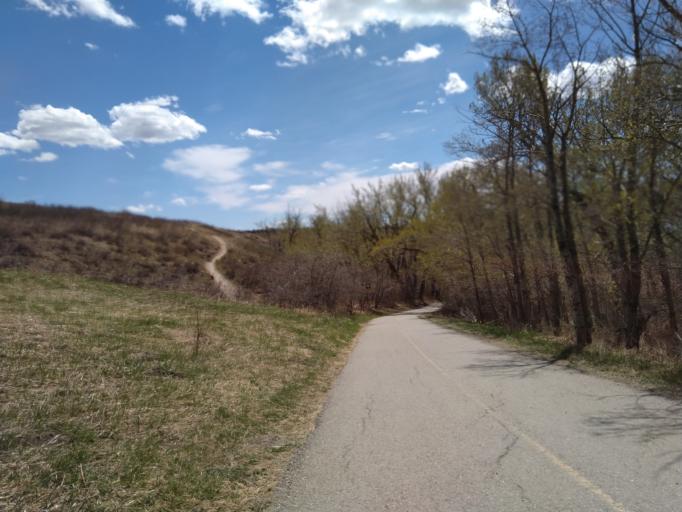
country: CA
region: Alberta
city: Calgary
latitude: 51.0937
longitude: -114.1829
